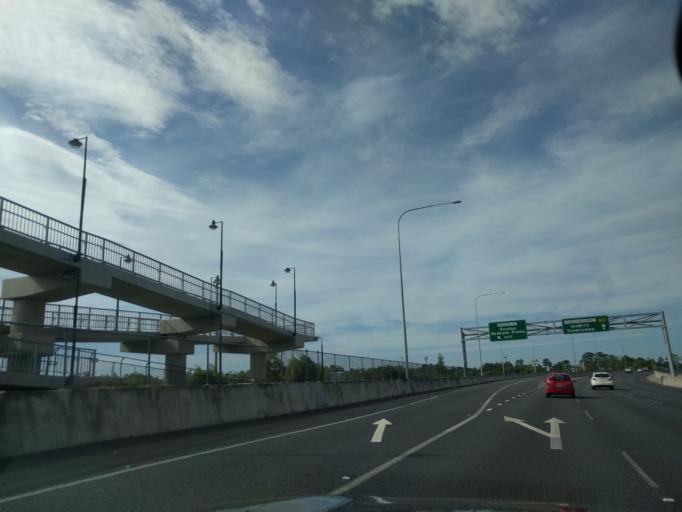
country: AU
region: Queensland
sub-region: Brisbane
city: Wacol
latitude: -27.6019
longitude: 152.9201
